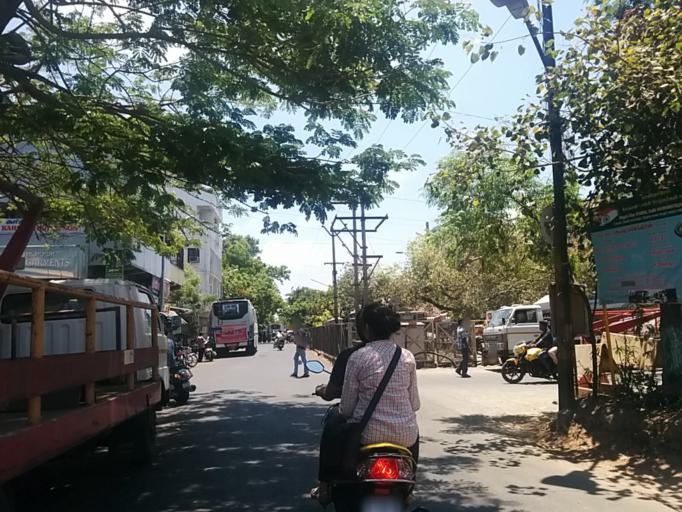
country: IN
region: Pondicherry
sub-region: Puducherry
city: Puducherry
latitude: 11.9356
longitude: 79.8329
